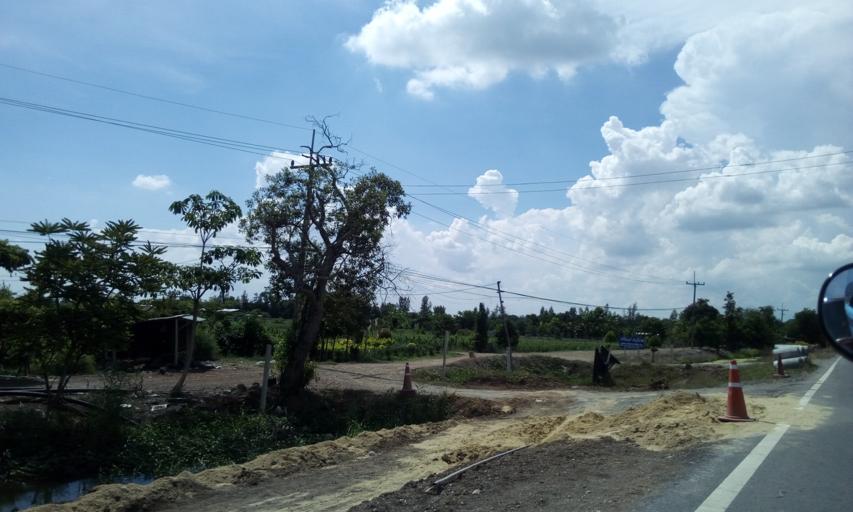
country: TH
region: Nakhon Nayok
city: Ongkharak
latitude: 14.0883
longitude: 100.9144
